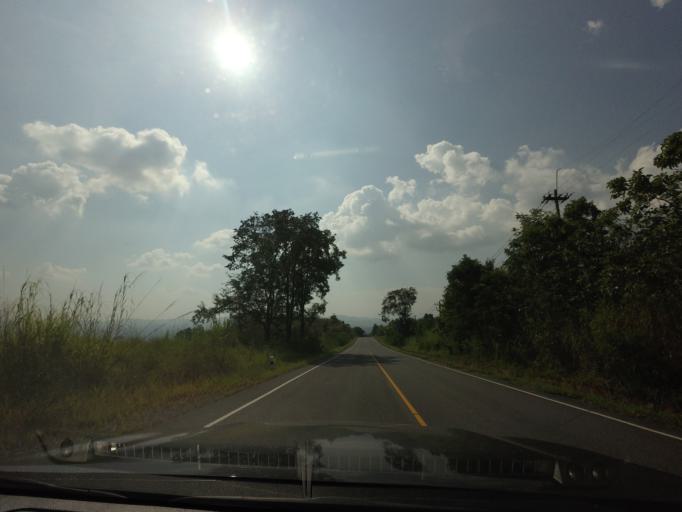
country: TH
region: Nan
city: Santi Suk
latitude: 18.9802
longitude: 100.9594
